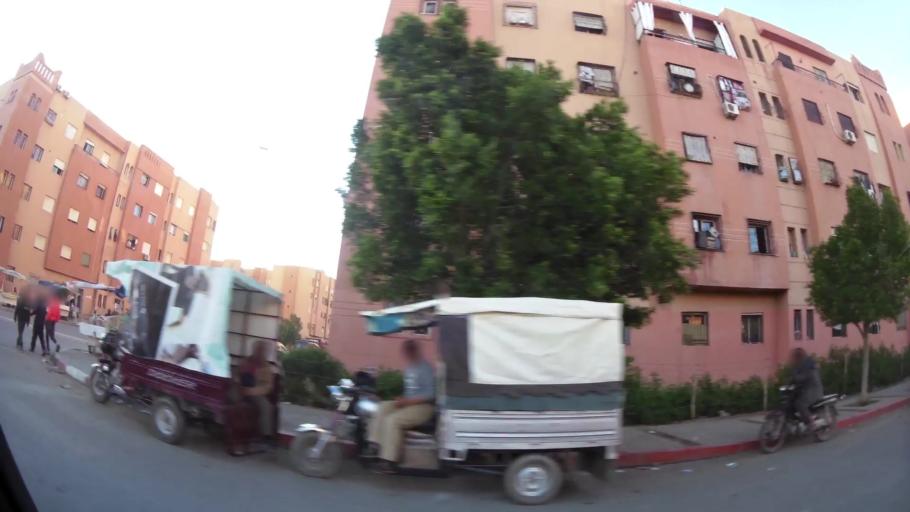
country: MA
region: Marrakech-Tensift-Al Haouz
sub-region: Marrakech
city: Marrakesh
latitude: 31.7491
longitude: -8.1172
